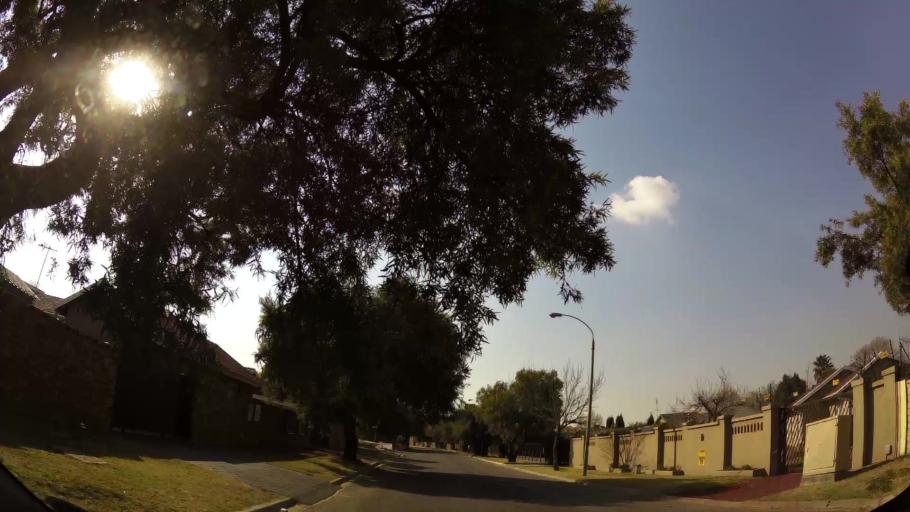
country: ZA
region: Gauteng
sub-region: Ekurhuleni Metropolitan Municipality
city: Benoni
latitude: -26.1541
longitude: 28.2823
